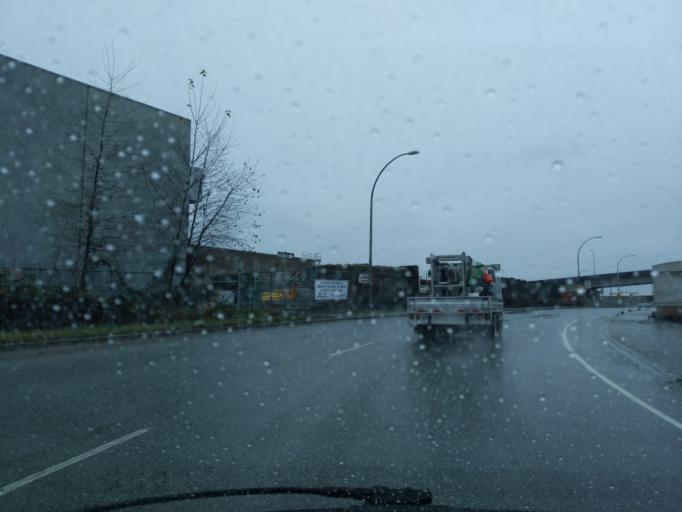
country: CA
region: British Columbia
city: Walnut Grove
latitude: 49.1812
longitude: -122.6669
